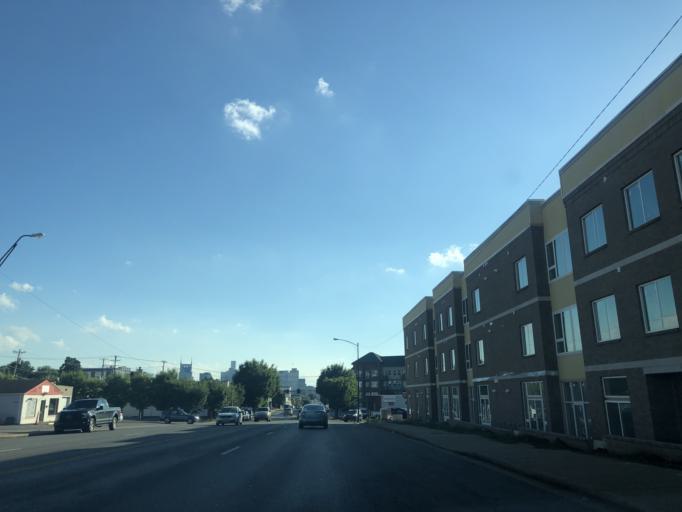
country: US
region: Tennessee
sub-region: Davidson County
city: Nashville
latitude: 36.1774
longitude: -86.7537
